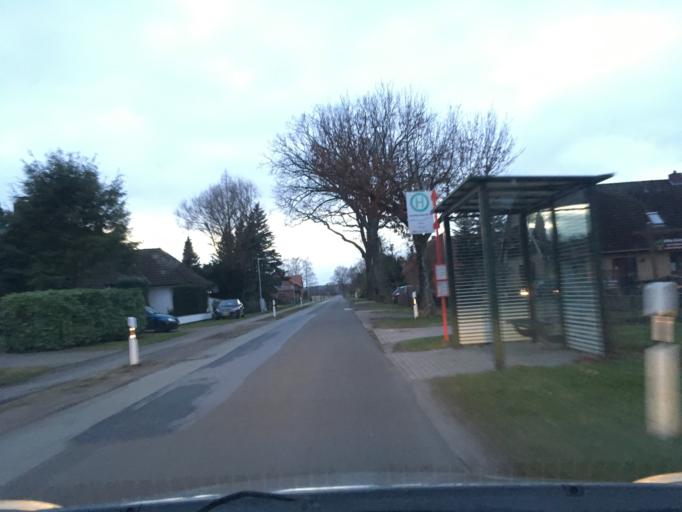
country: DE
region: Lower Saxony
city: Winsen
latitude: 53.3561
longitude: 10.1786
